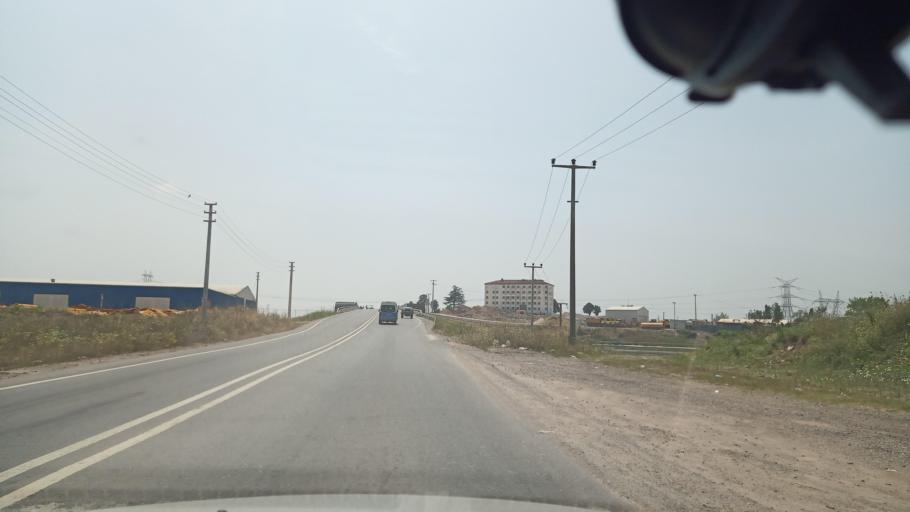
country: TR
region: Sakarya
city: Adapazari
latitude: 40.8266
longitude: 30.3966
